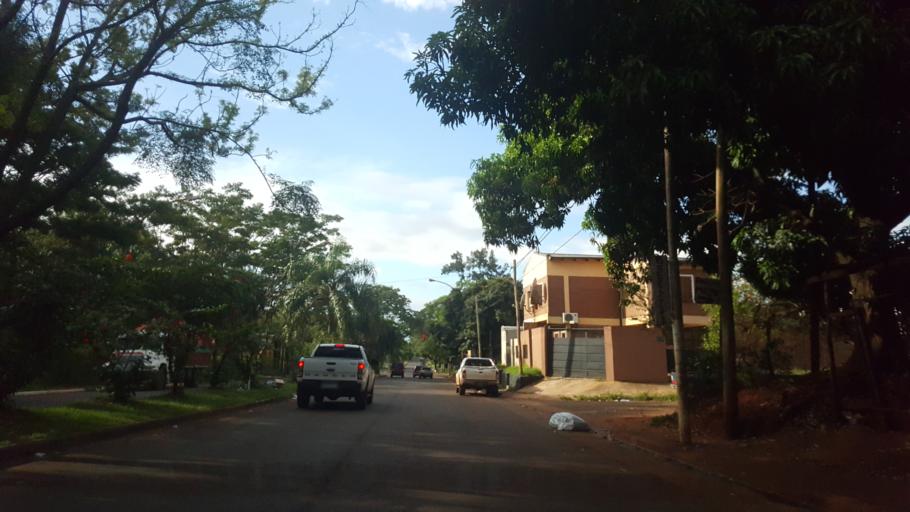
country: AR
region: Misiones
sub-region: Departamento de Capital
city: Posadas
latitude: -27.3651
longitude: -55.9314
